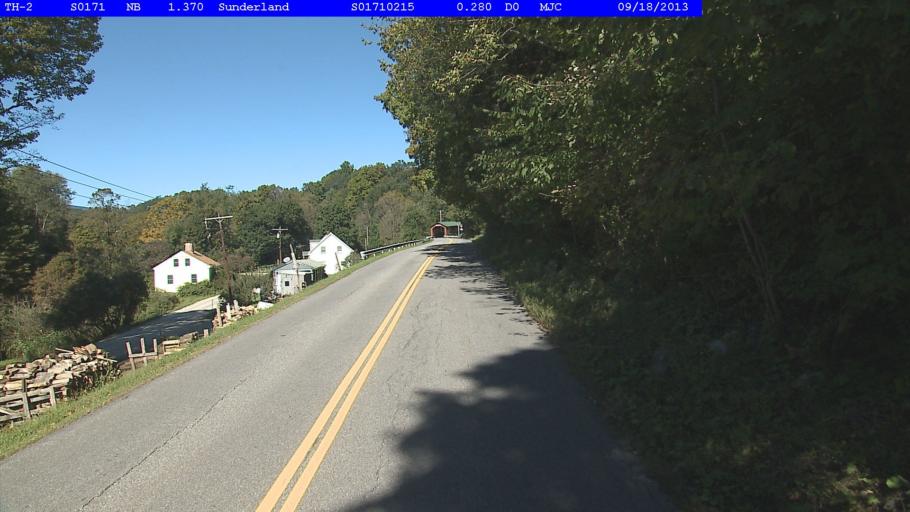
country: US
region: Vermont
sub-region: Bennington County
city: Arlington
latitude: 43.0709
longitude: -73.1346
